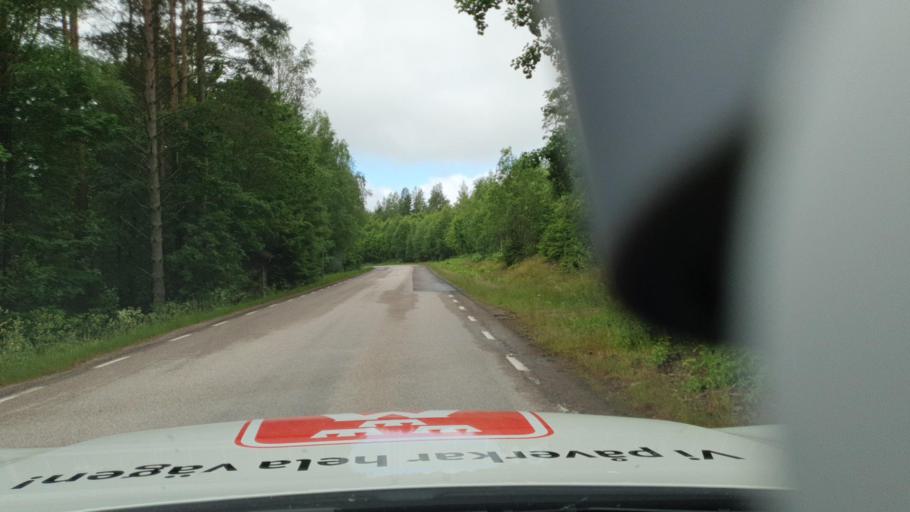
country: SE
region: Vaermland
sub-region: Kristinehamns Kommun
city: Bjorneborg
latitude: 59.1044
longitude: 14.3280
